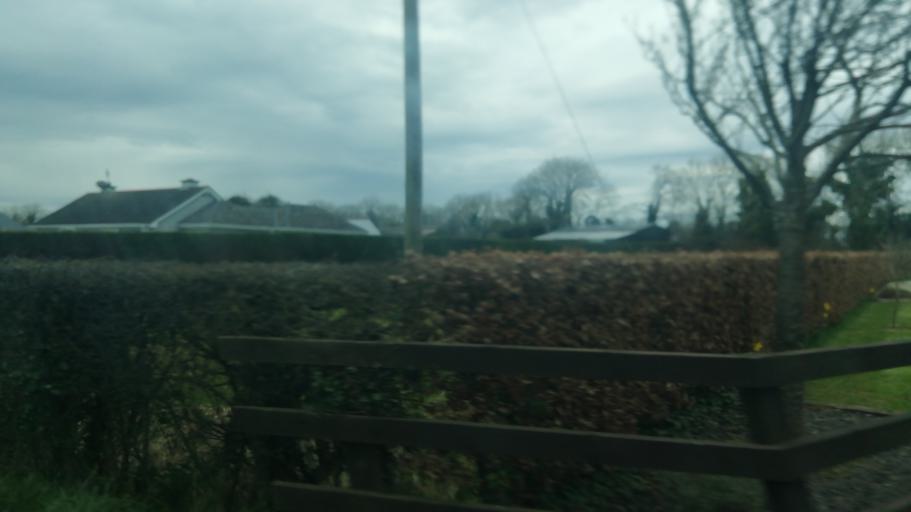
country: IE
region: Leinster
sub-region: Kildare
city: Derrinturn
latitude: 53.2830
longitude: -6.8876
